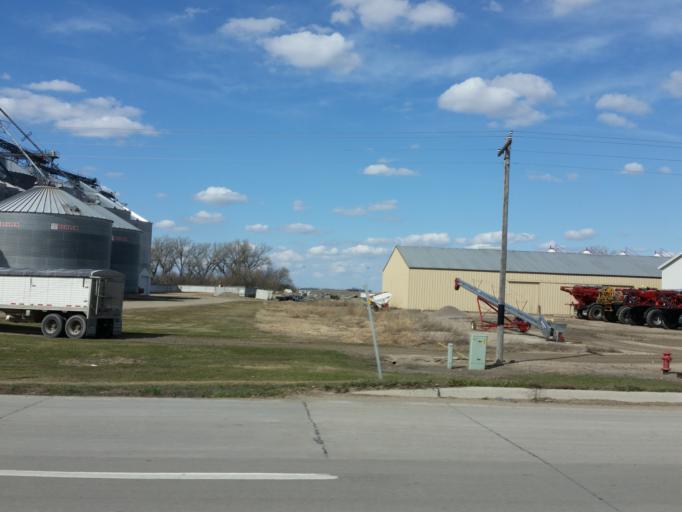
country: US
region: Minnesota
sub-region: Lac qui Parle County
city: Dawson
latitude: 44.9357
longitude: -96.0687
